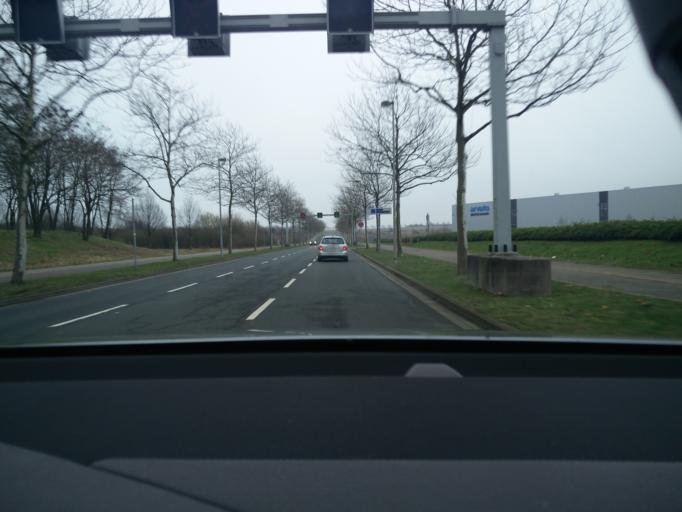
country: DE
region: Lower Saxony
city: Laatzen
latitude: 52.3312
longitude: 9.8203
